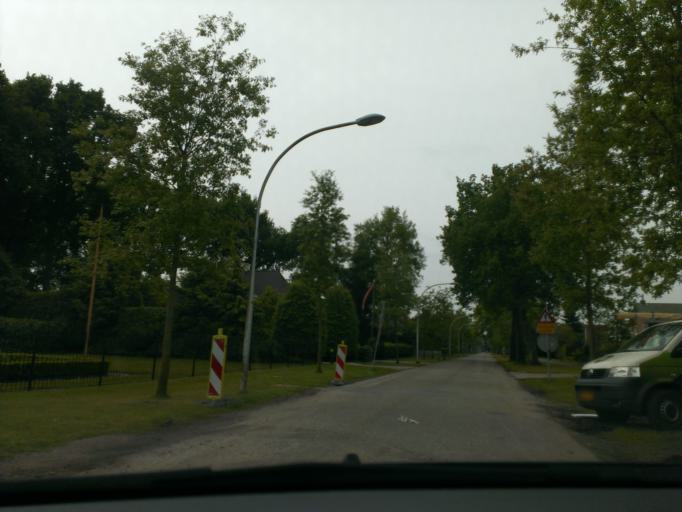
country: NL
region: Overijssel
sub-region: Gemeente Almelo
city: Almelo
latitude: 52.3366
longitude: 6.6643
